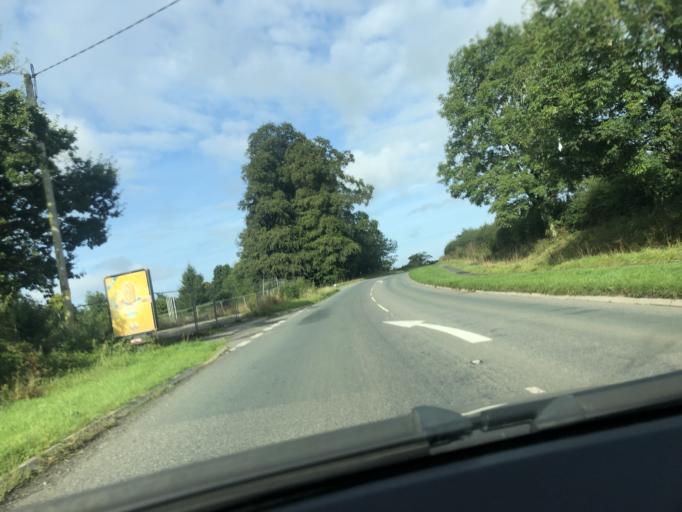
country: GB
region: England
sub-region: Cornwall
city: Launceston
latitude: 50.6445
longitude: -4.2917
